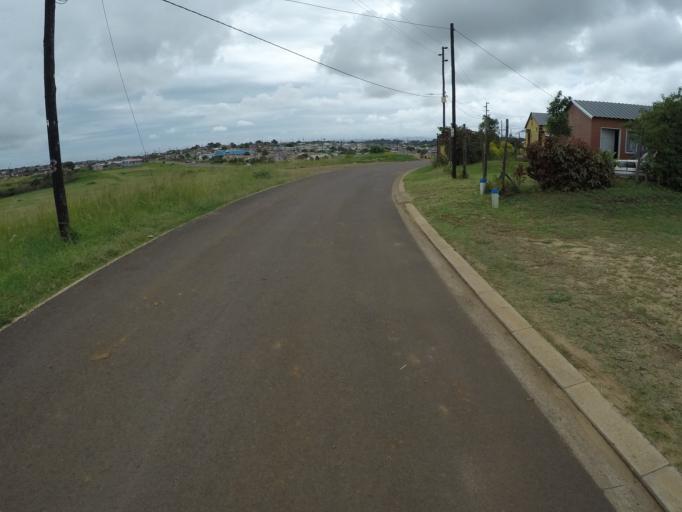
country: ZA
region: KwaZulu-Natal
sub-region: uThungulu District Municipality
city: Empangeni
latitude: -28.7660
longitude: 31.8810
